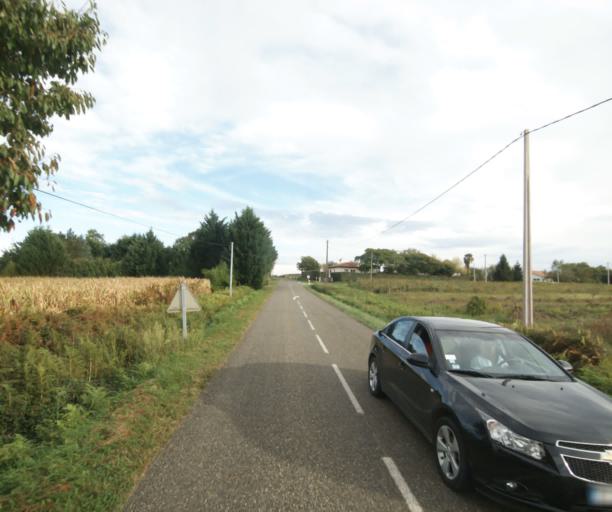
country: FR
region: Midi-Pyrenees
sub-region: Departement du Gers
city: Le Houga
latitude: 43.8563
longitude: -0.1420
